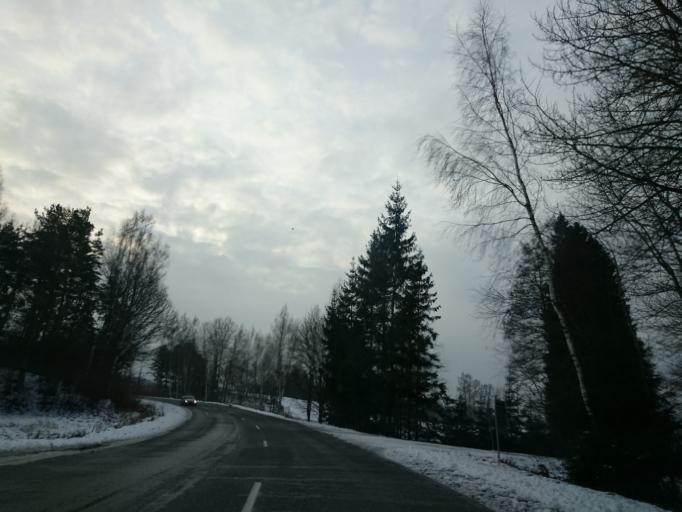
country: LV
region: Seja
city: Loja
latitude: 57.1908
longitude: 24.5969
